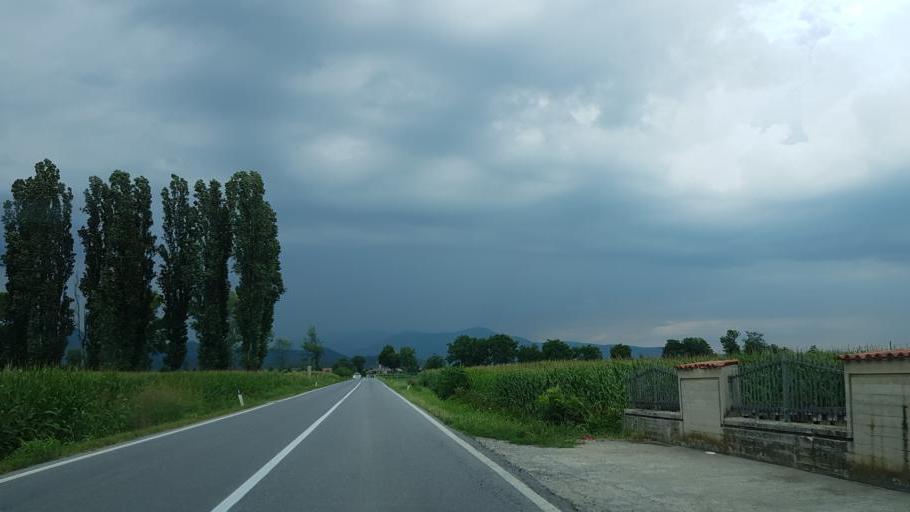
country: IT
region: Piedmont
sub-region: Provincia di Cuneo
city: San Rocco
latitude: 44.3960
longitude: 7.4536
